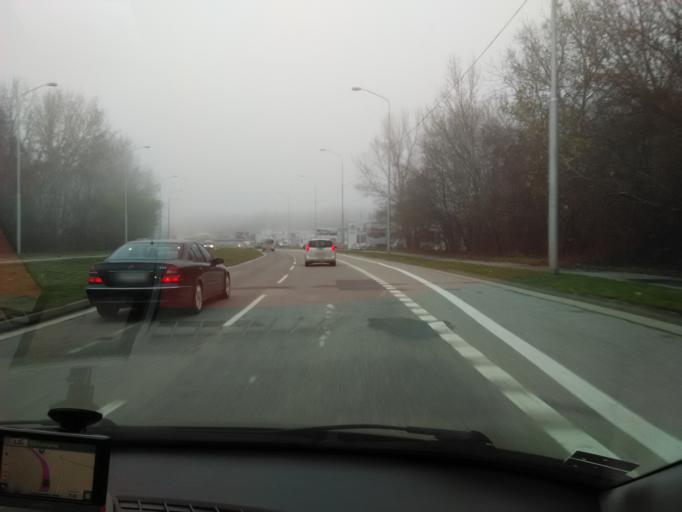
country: SK
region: Bratislavsky
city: Bratislava
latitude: 48.1192
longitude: 17.1351
